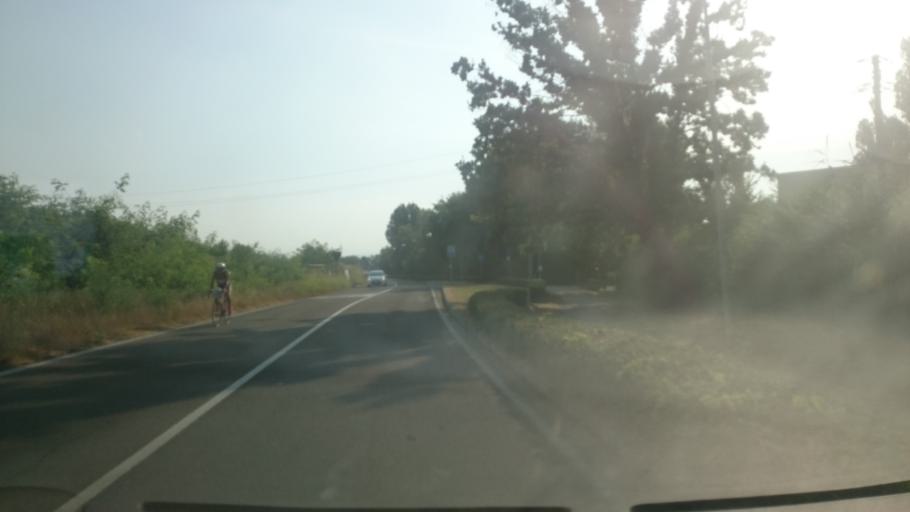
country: IT
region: Emilia-Romagna
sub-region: Provincia di Reggio Emilia
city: Rubiera
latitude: 44.6423
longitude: 10.7791
